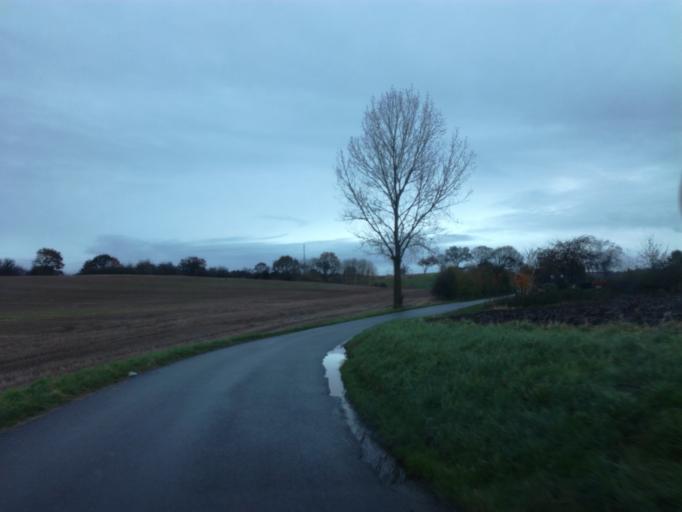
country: DK
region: South Denmark
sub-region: Vejle Kommune
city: Borkop
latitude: 55.6556
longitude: 9.6426
